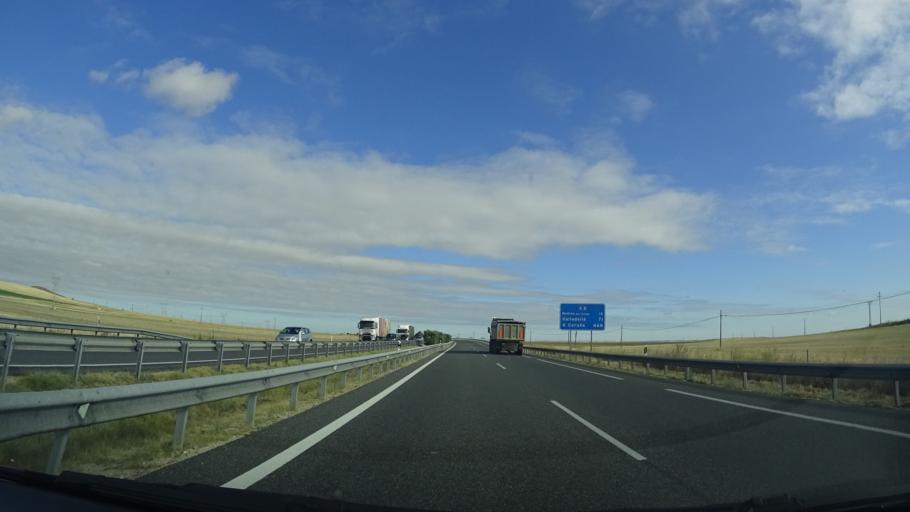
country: ES
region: Castille and Leon
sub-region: Provincia de Valladolid
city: Ataquines
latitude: 41.1871
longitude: -4.8105
